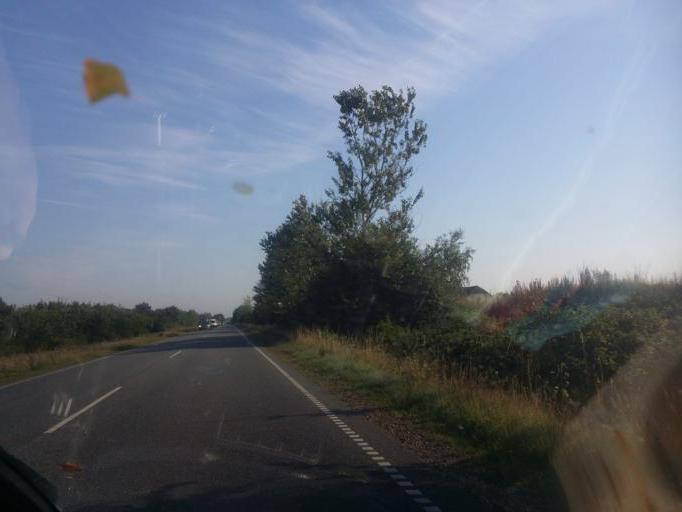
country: DK
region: South Denmark
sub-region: Esbjerg Kommune
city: Ribe
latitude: 55.2993
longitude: 8.7423
